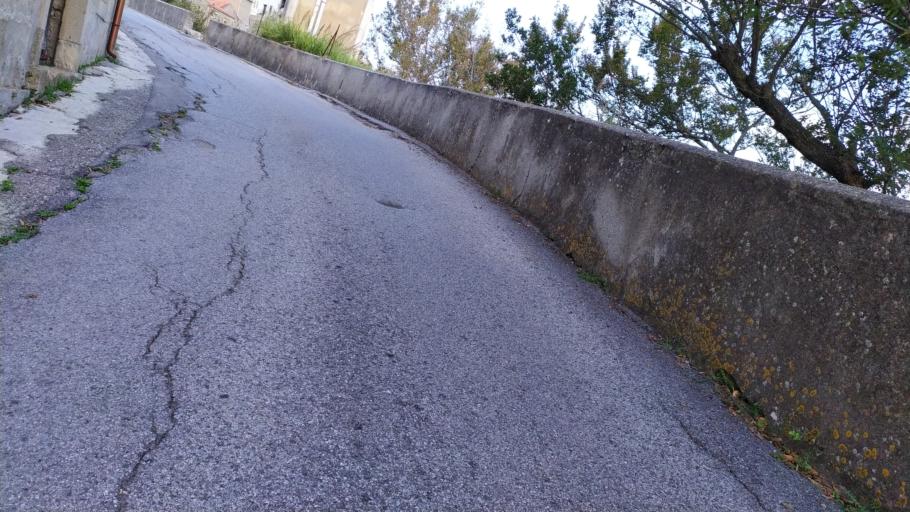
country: IT
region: Sicily
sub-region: Messina
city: Rometta
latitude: 38.1700
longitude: 15.4156
